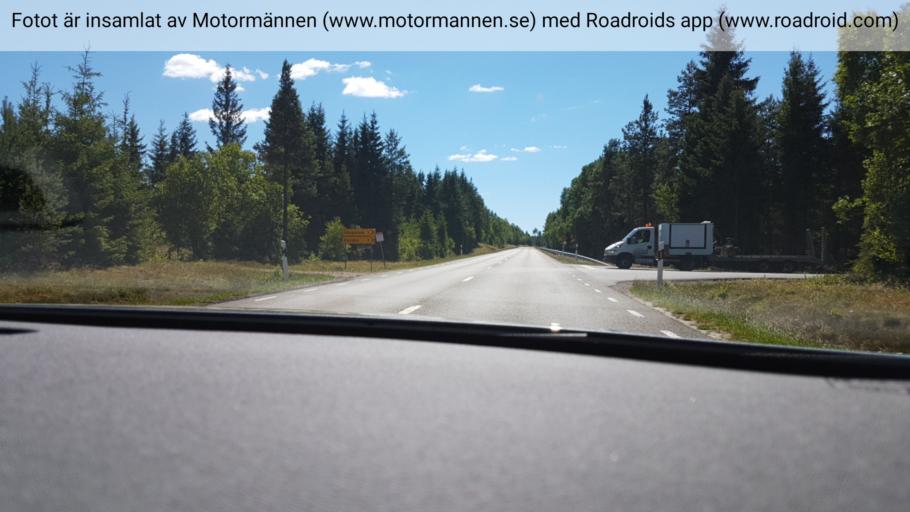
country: SE
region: Joenkoeping
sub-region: Gnosjo Kommun
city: Marieholm
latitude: 57.6245
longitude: 13.7737
